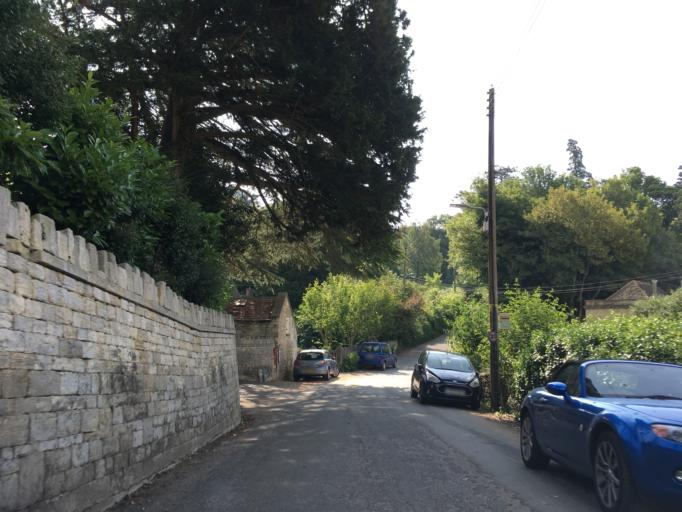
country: GB
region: England
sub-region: Gloucestershire
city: Brimscombe
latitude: 51.7261
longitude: -2.1976
